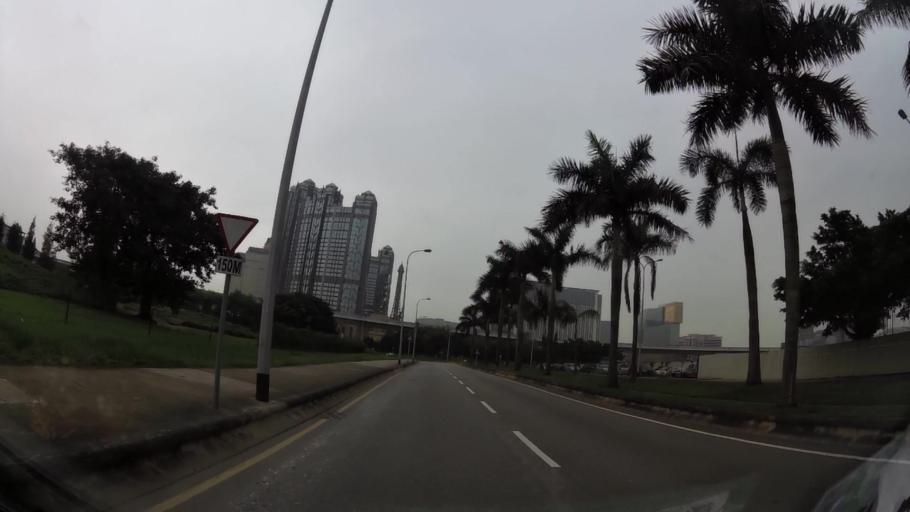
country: MO
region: Macau
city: Macau
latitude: 22.1372
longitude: 113.5631
